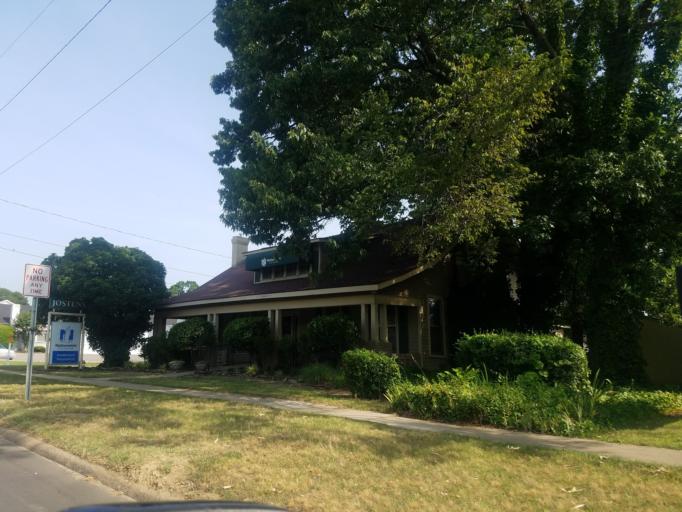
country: US
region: Arkansas
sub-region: Pope County
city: Russellville
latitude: 35.2796
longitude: -93.1386
